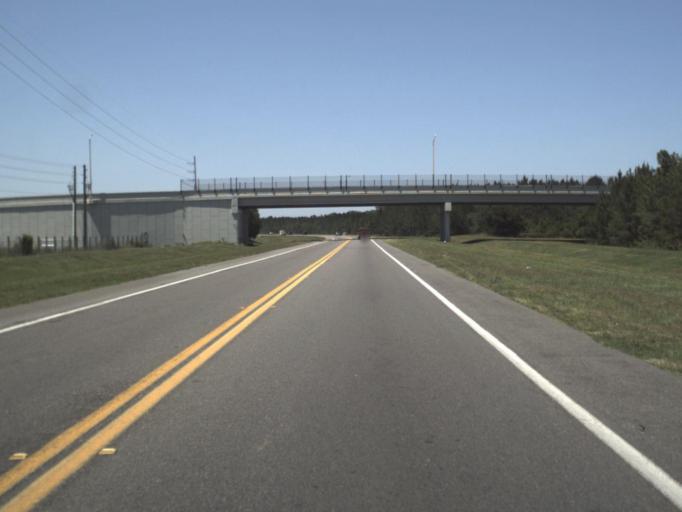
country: US
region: Florida
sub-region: Clay County
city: Lakeside
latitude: 30.1703
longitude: -81.8313
